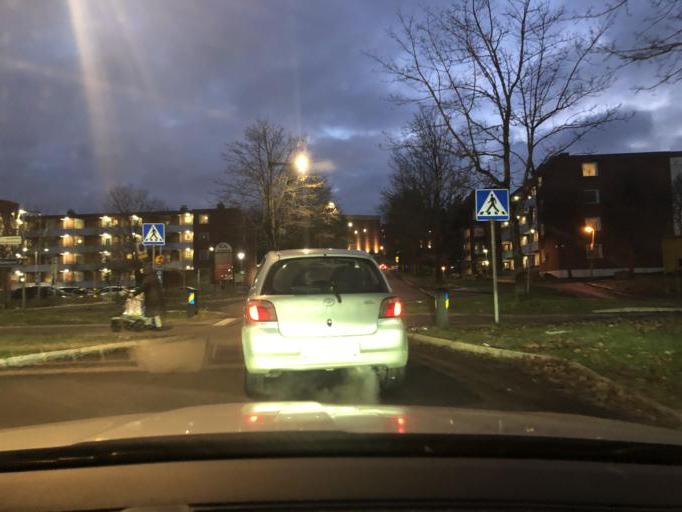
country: SE
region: Stockholm
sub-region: Botkyrka Kommun
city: Fittja
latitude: 59.2650
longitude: 17.8877
